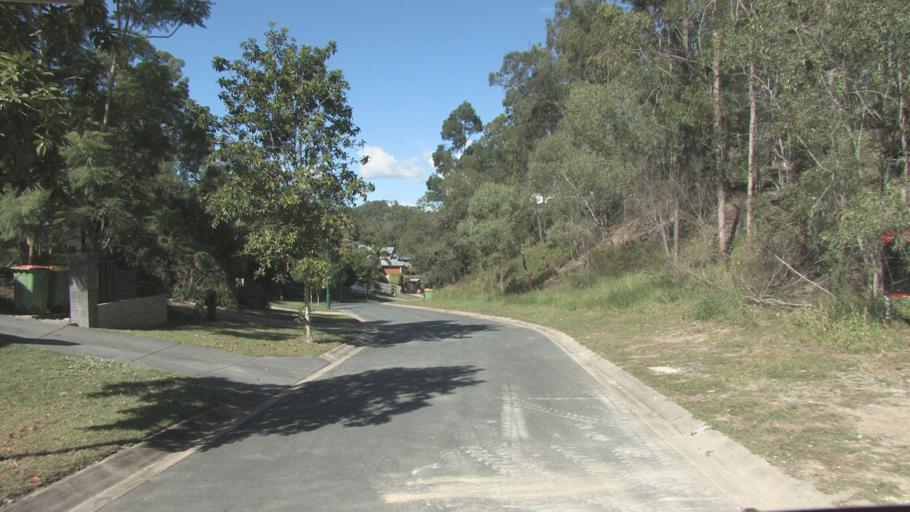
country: AU
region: Queensland
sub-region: Logan
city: Slacks Creek
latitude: -27.6488
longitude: 153.1879
